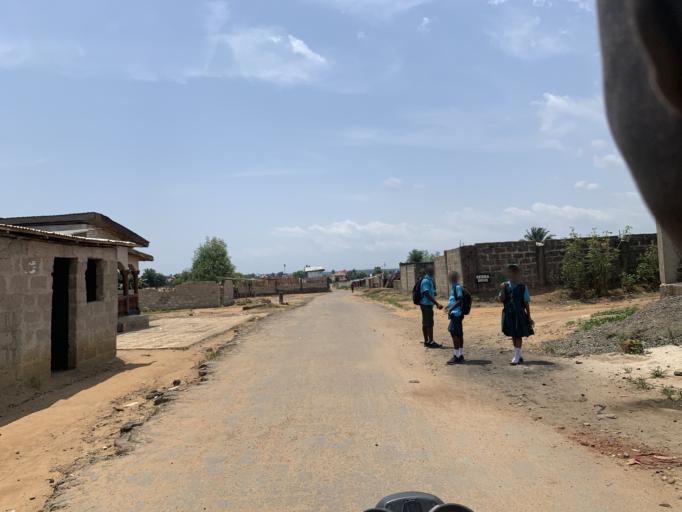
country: SL
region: Western Area
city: Waterloo
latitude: 8.3374
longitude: -13.0325
